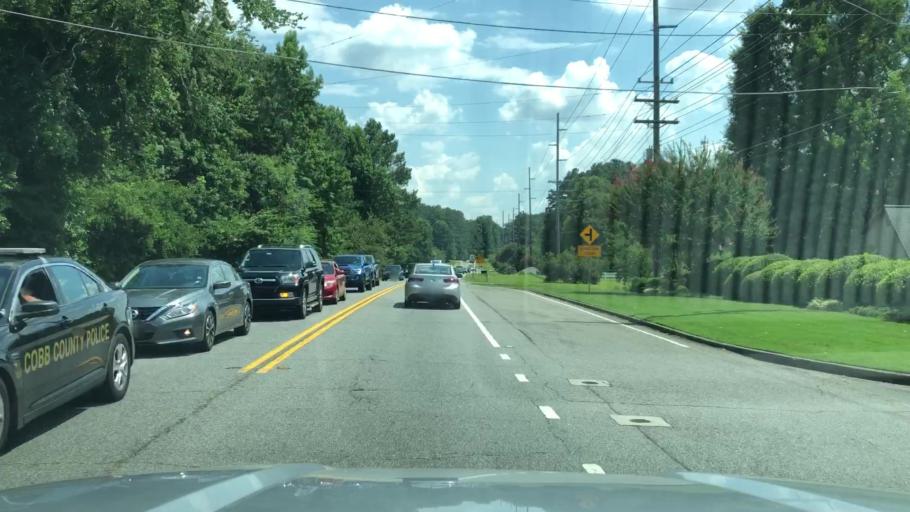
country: US
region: Georgia
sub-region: Cobb County
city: Acworth
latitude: 34.0112
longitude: -84.6990
